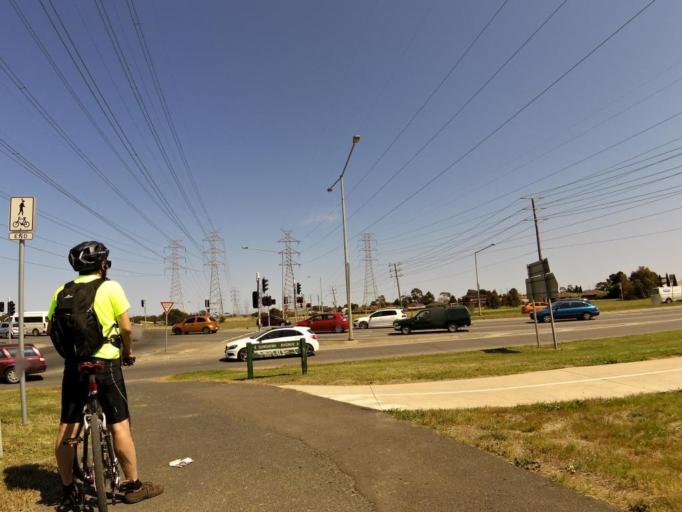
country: AU
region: Victoria
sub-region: Brimbank
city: Kealba
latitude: -37.7496
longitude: 144.8322
